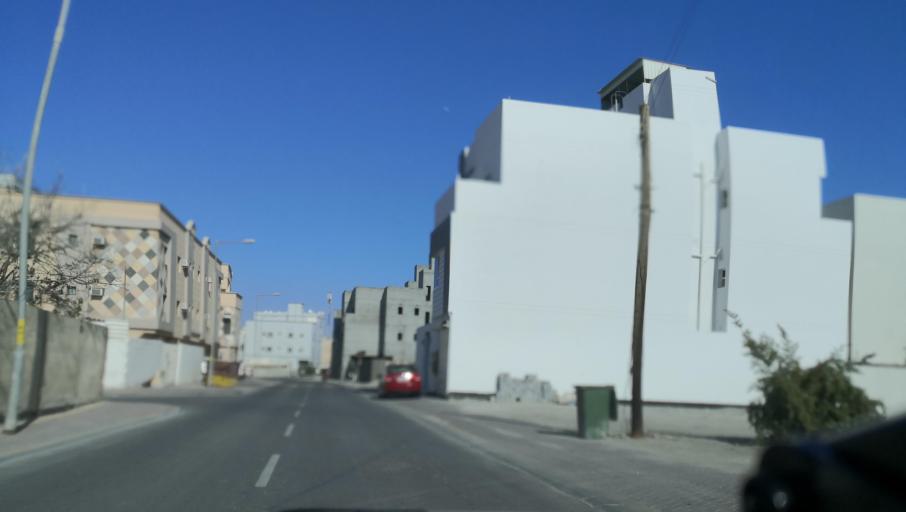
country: BH
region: Muharraq
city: Al Hadd
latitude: 26.2527
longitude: 50.6343
